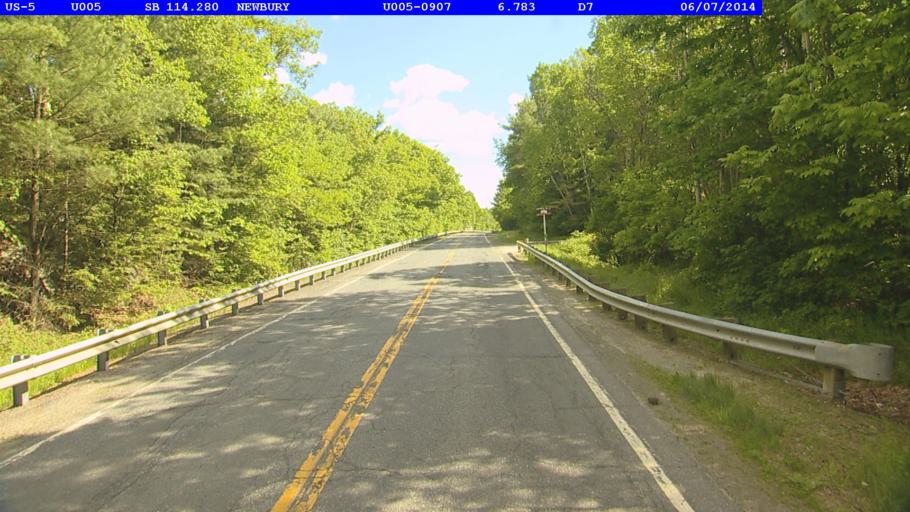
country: US
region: New Hampshire
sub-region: Grafton County
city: Woodsville
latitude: 44.1178
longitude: -72.0542
